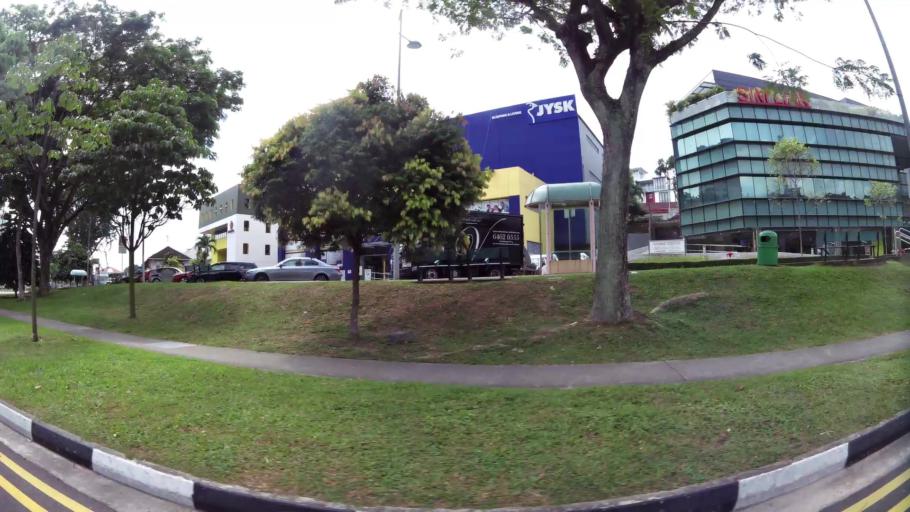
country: SG
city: Singapore
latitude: 1.3446
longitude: 103.7749
